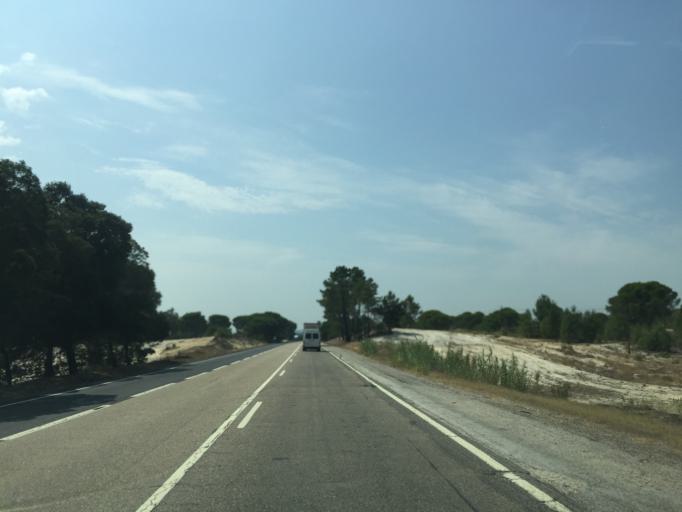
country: PT
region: Setubal
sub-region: Grandola
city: Grandola
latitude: 38.2514
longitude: -8.5477
